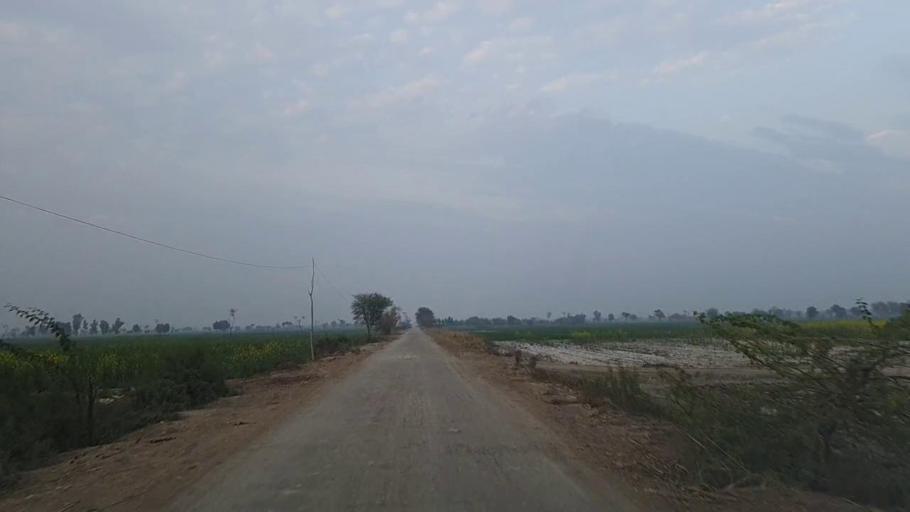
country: PK
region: Sindh
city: Jam Sahib
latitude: 26.3019
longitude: 68.5936
